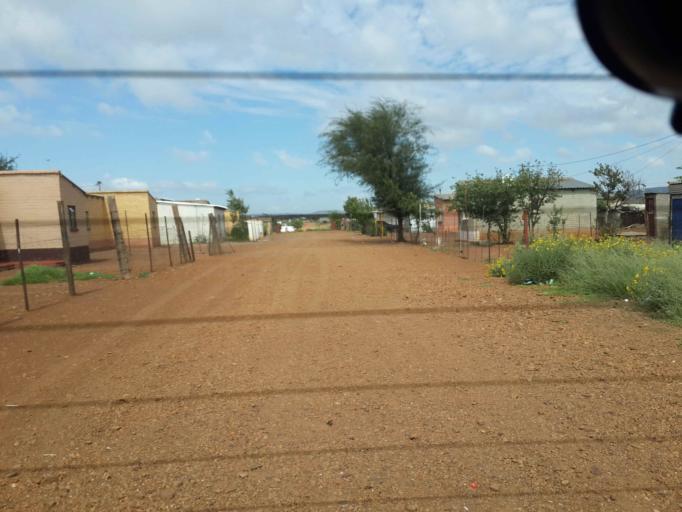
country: ZA
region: Northern Cape
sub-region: Siyanda District Municipality
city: Danielskuil
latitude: -28.1961
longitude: 23.5539
